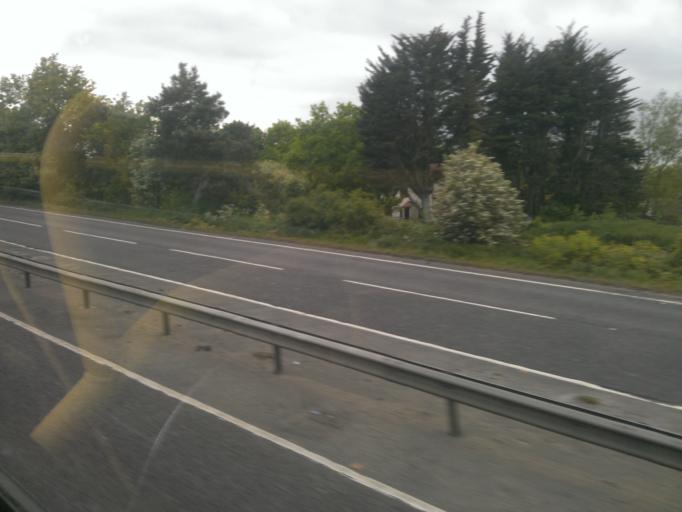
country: GB
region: England
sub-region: Essex
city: Colchester
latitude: 51.9312
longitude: 0.9445
